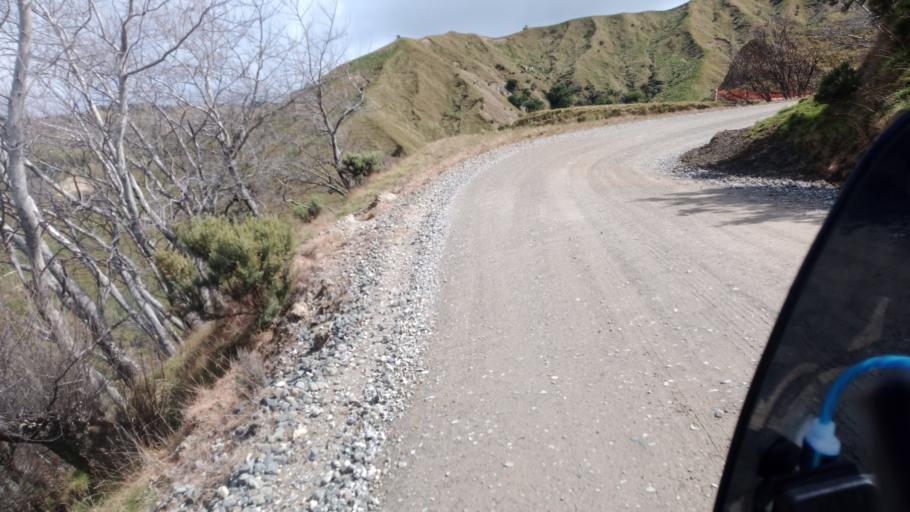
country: NZ
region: Gisborne
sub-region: Gisborne District
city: Gisborne
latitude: -38.5596
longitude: 178.1555
